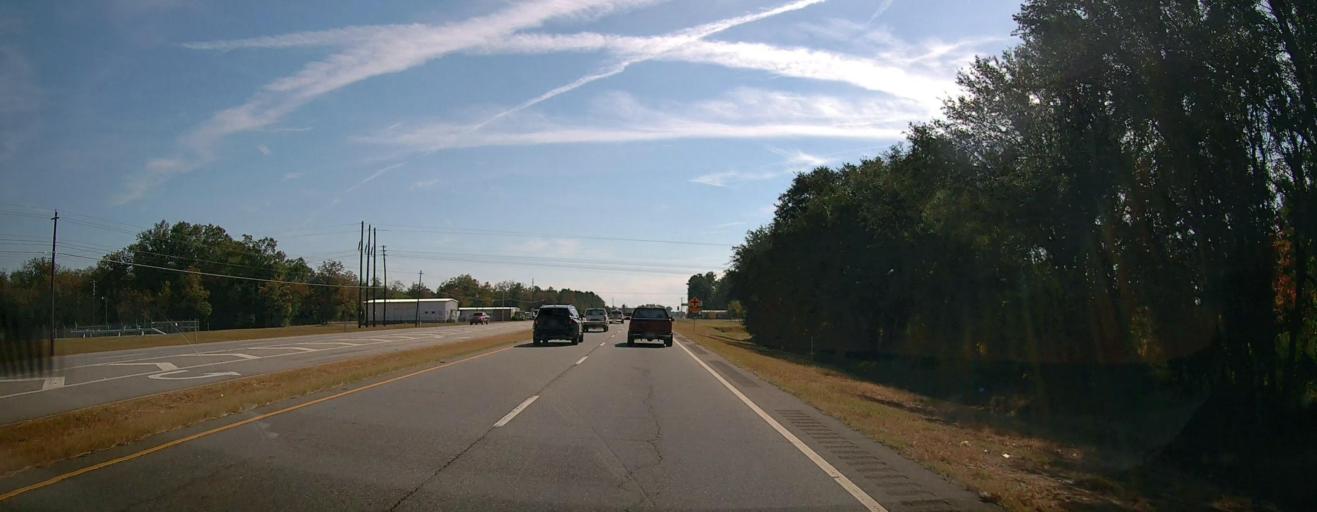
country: US
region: Georgia
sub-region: Dougherty County
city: Putney
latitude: 31.5022
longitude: -84.1156
